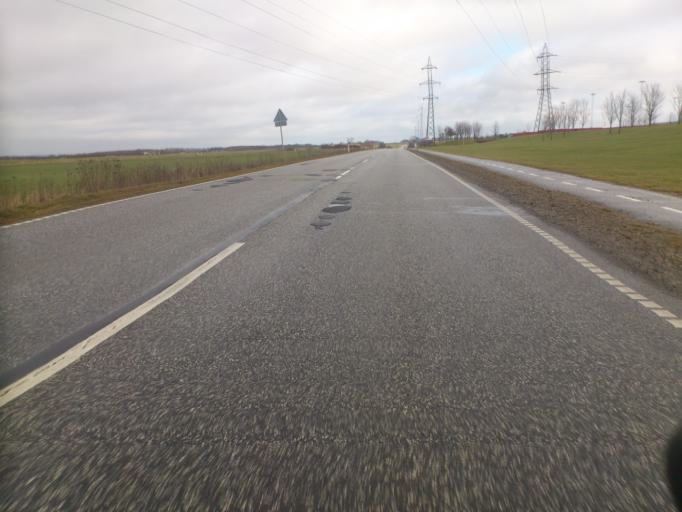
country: DK
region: South Denmark
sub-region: Fredericia Kommune
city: Fredericia
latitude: 55.5910
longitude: 9.7176
